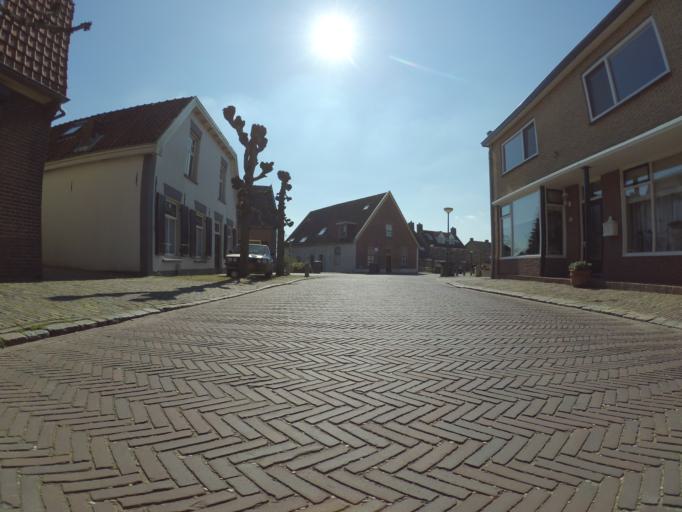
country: NL
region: Utrecht
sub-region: Gemeente Utrechtse Heuvelrug
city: Driebergen-Rijsenburg
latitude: 52.0232
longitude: 5.2453
